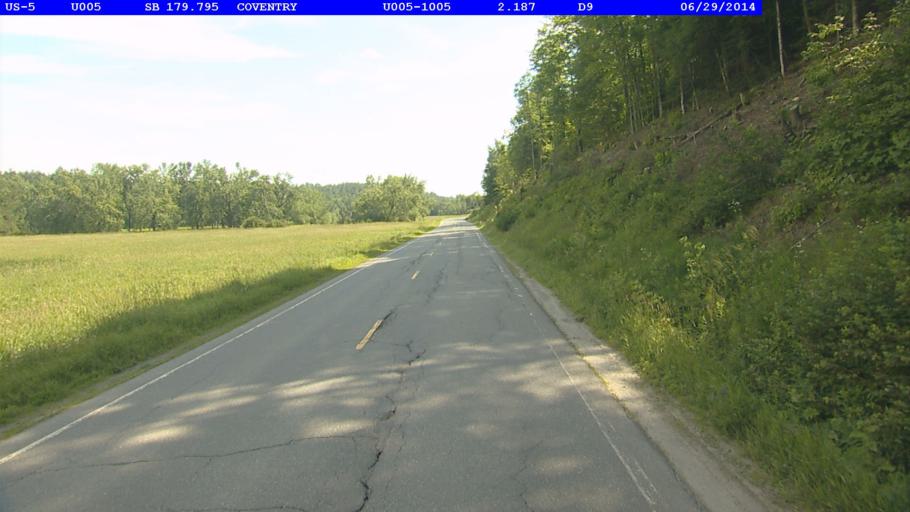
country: US
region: Vermont
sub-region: Orleans County
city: Newport
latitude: 44.8868
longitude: -72.2479
